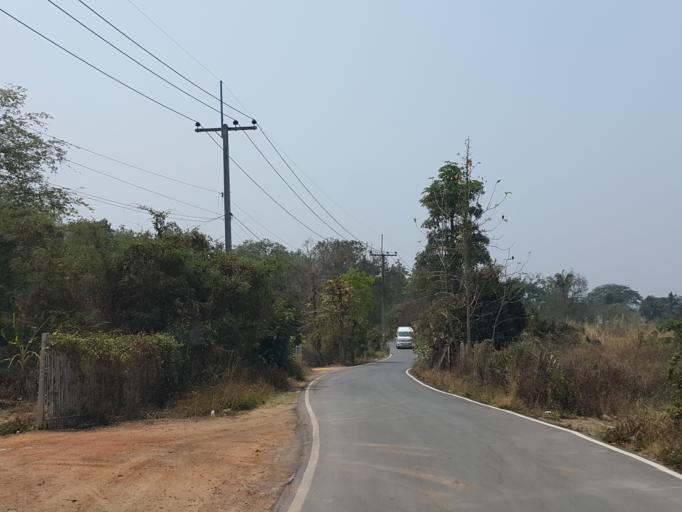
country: TH
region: Chiang Mai
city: San Kamphaeng
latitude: 18.7183
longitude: 99.1739
